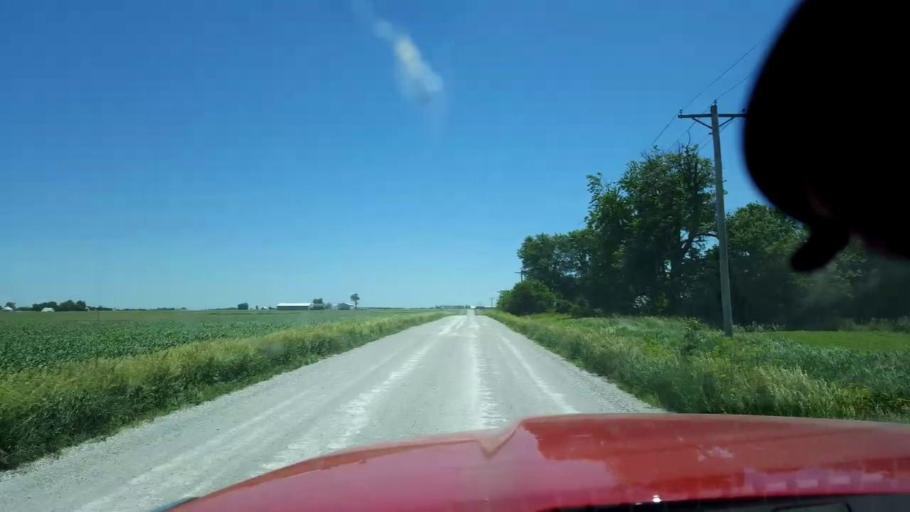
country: US
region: Iowa
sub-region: Washington County
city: Washington
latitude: 41.2799
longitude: -91.6550
